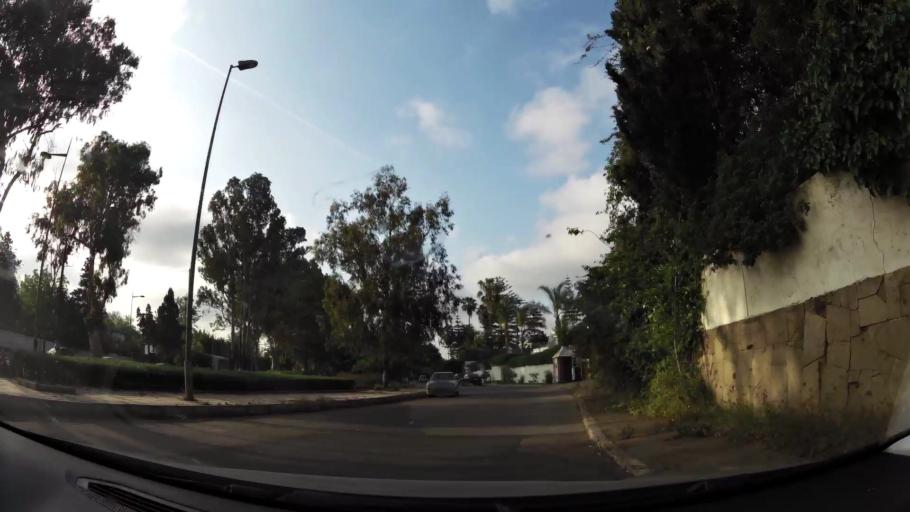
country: MA
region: Rabat-Sale-Zemmour-Zaer
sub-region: Rabat
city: Rabat
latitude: 33.9481
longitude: -6.8227
